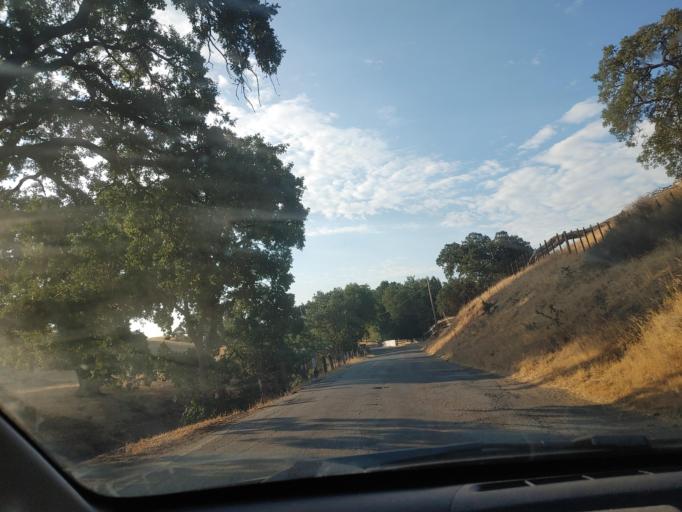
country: US
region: California
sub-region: San Benito County
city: Ridgemark
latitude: 36.7979
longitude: -121.2654
